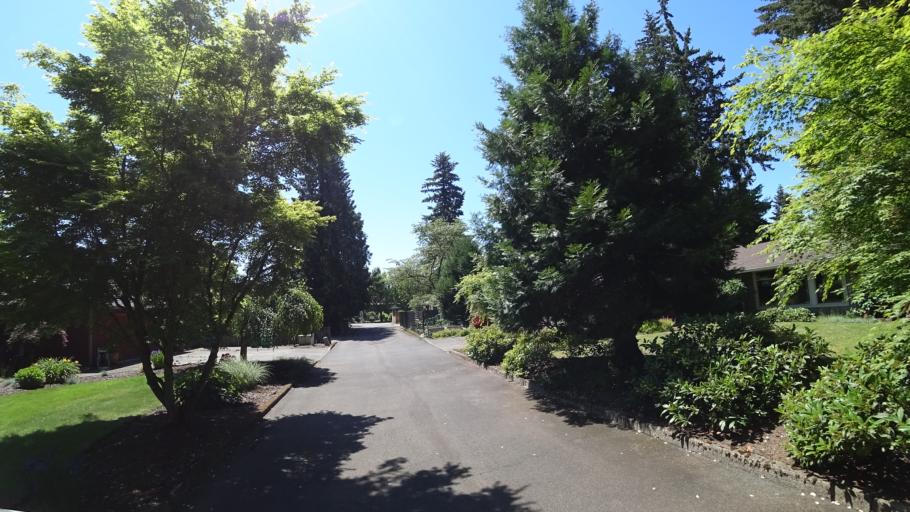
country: US
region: Oregon
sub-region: Clackamas County
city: Happy Valley
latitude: 45.4807
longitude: -122.5282
